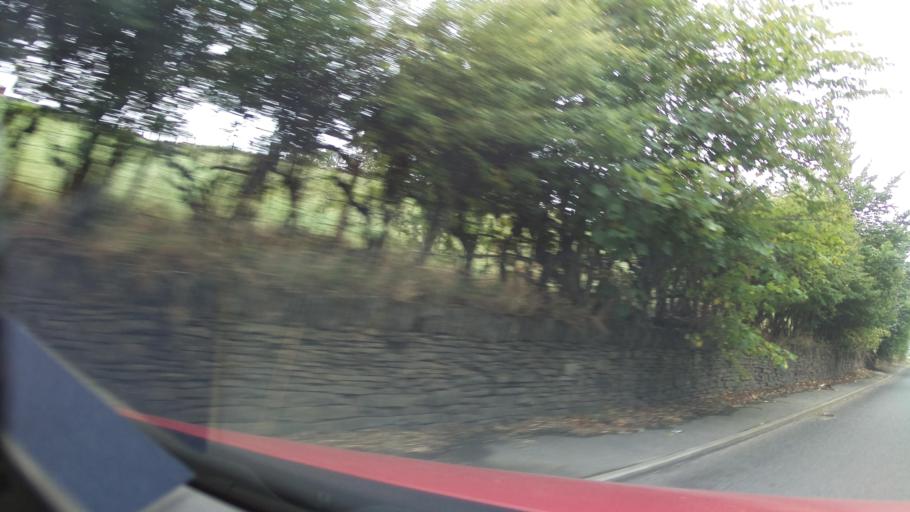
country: GB
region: England
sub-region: Kirklees
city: Kirkburton
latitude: 53.5765
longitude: -1.7139
